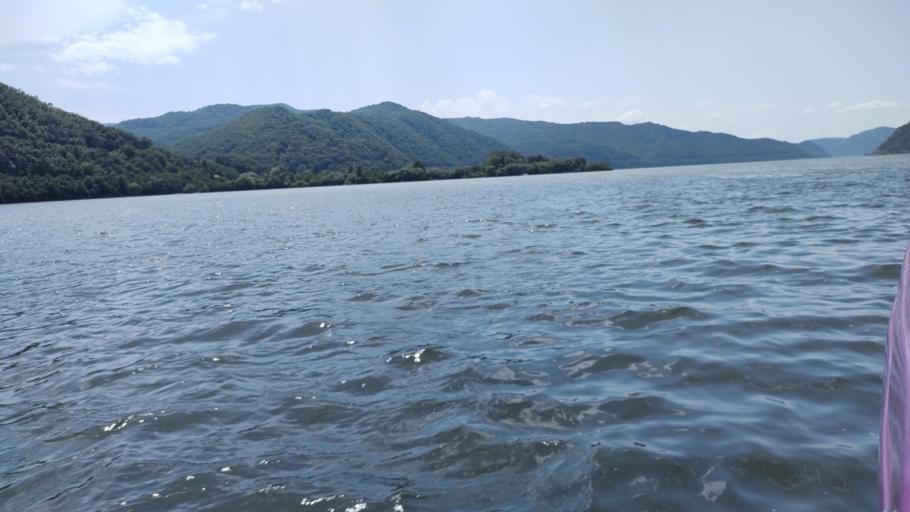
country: RO
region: Caras-Severin
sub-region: Comuna Berzasca
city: Liubcova
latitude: 44.6526
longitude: 21.8530
